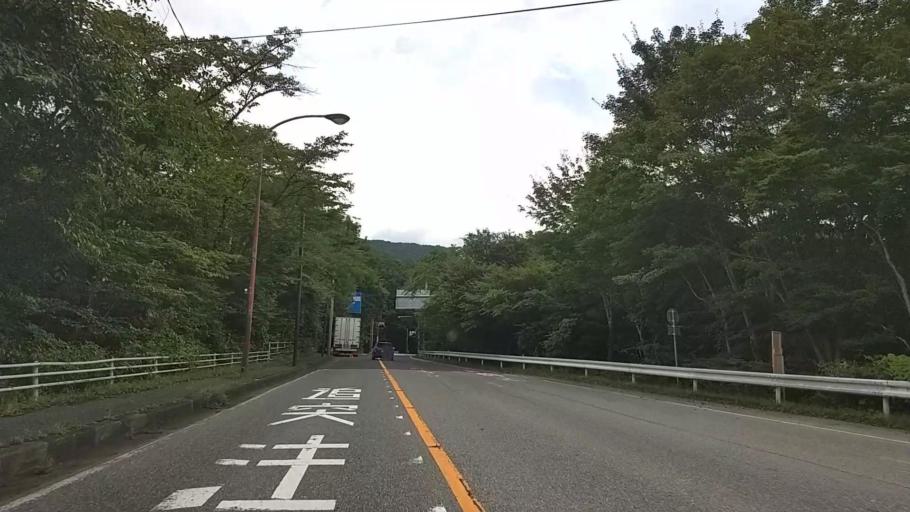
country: JP
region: Tochigi
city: Nikko
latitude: 36.7426
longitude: 139.5667
